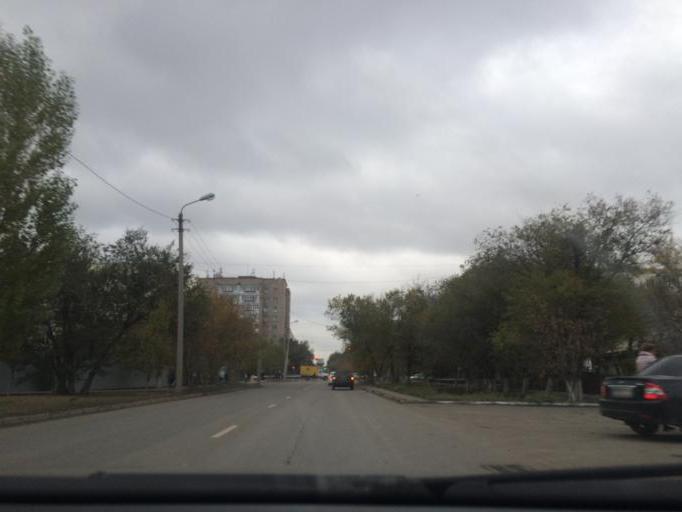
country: KZ
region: Astana Qalasy
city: Astana
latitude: 51.1954
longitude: 71.3904
